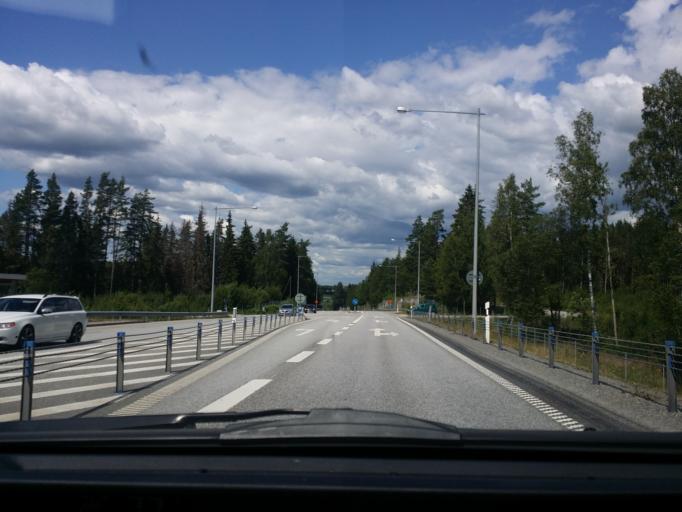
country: SE
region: OErebro
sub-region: Orebro Kommun
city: Hovsta
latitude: 59.3835
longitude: 15.2167
